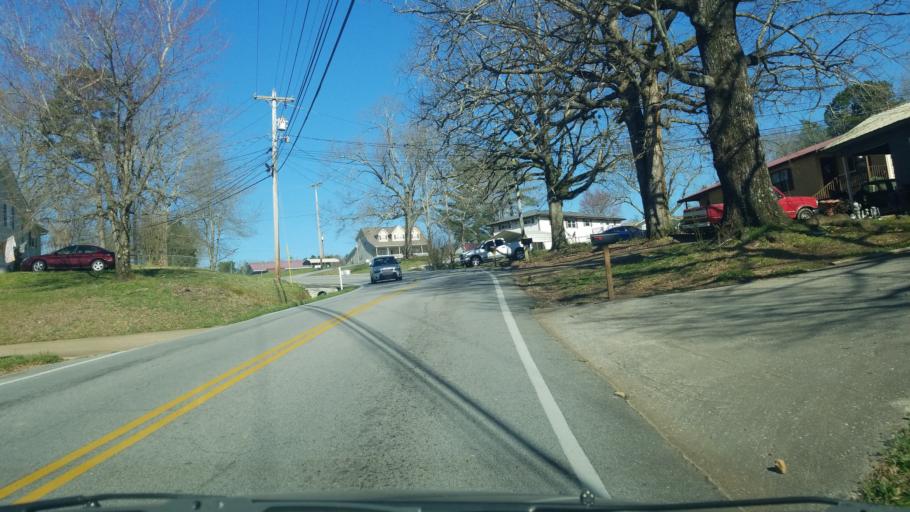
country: US
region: Tennessee
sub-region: Hamilton County
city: Middle Valley
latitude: 35.2144
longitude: -85.1778
